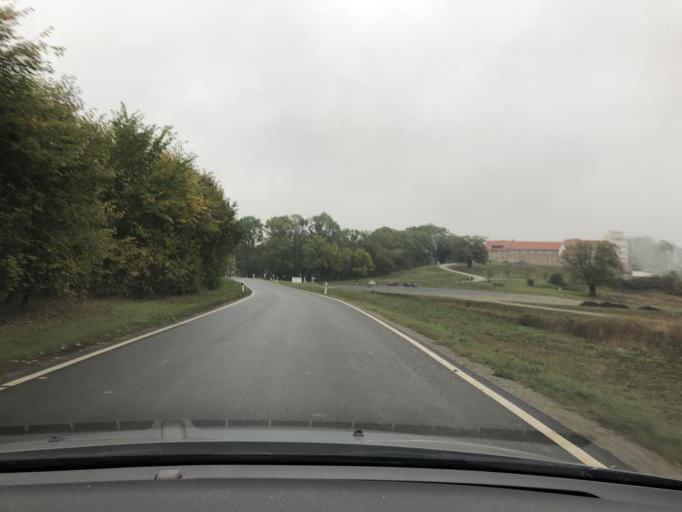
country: DE
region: Thuringia
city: Kreuzebra
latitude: 51.3620
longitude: 10.2644
